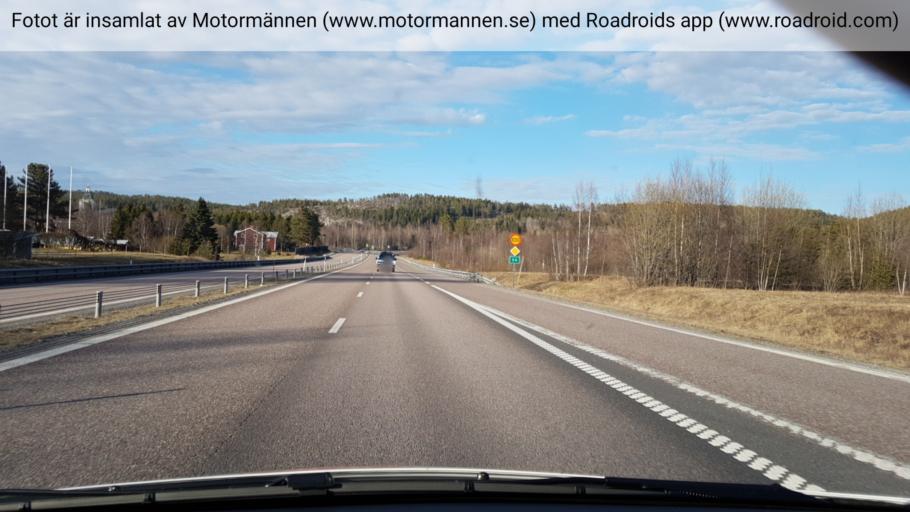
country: SE
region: Vaesternorrland
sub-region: OErnskoeldsviks Kommun
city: Ornskoldsvik
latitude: 63.3116
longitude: 18.7883
